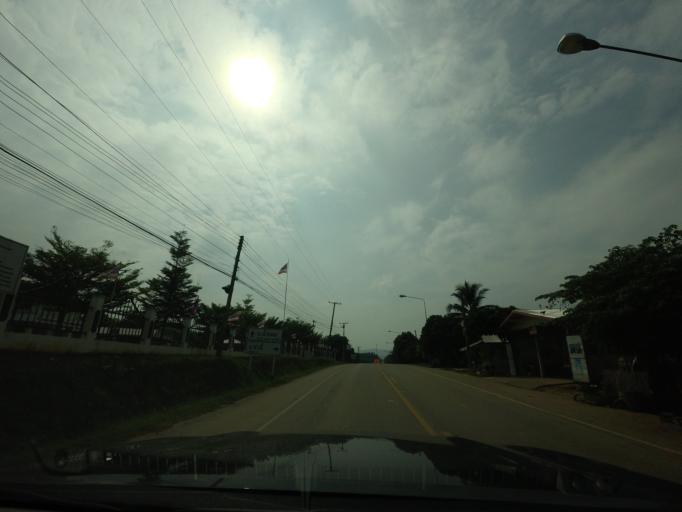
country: TH
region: Loei
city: Chiang Khan
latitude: 17.7806
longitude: 101.5773
